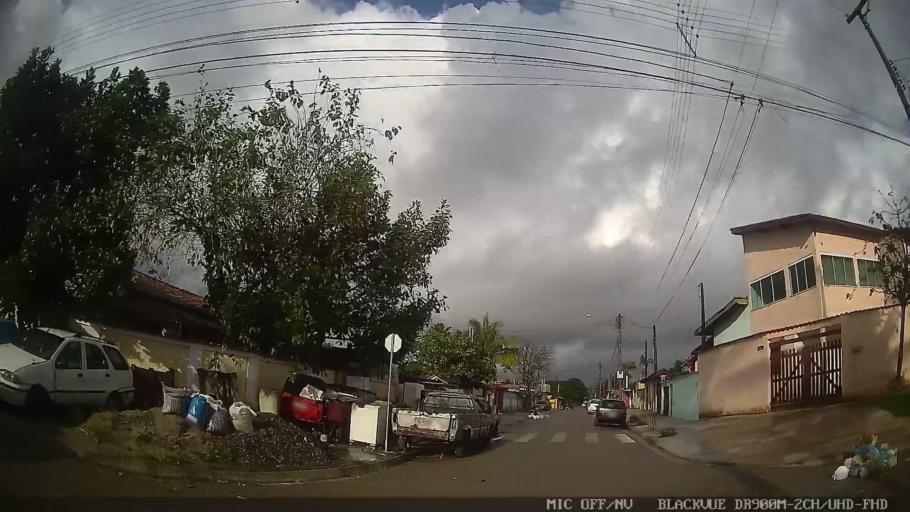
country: BR
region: Sao Paulo
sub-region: Itanhaem
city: Itanhaem
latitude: -24.2101
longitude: -46.8783
